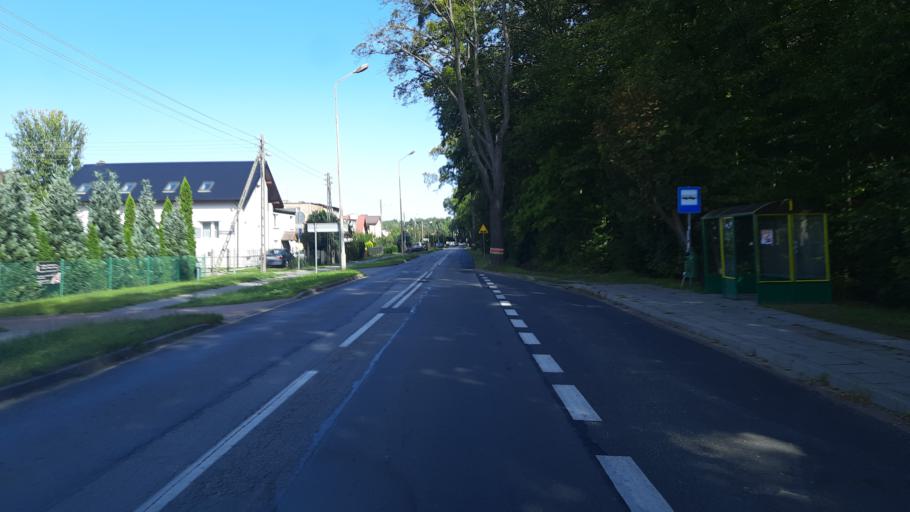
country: PL
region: Lower Silesian Voivodeship
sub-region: Powiat wroclawski
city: Dlugoleka
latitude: 51.1792
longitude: 17.1904
